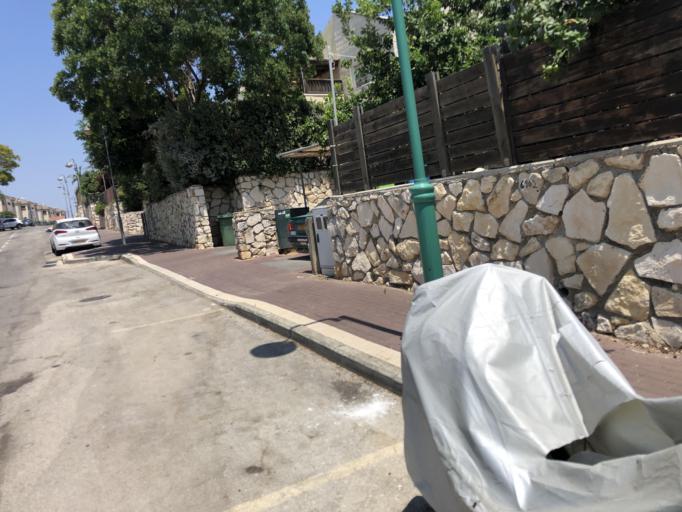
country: IL
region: Haifa
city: Daliyat el Karmil
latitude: 32.6388
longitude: 35.0884
